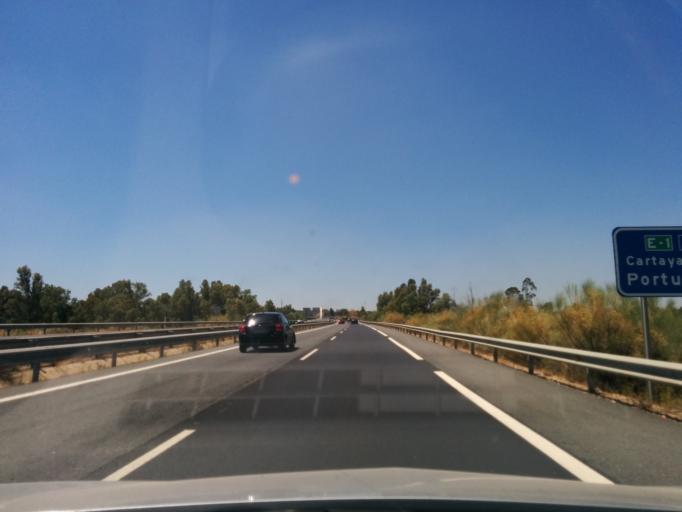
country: ES
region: Andalusia
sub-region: Provincia de Huelva
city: Gibraleon
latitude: 37.3544
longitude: -6.9722
